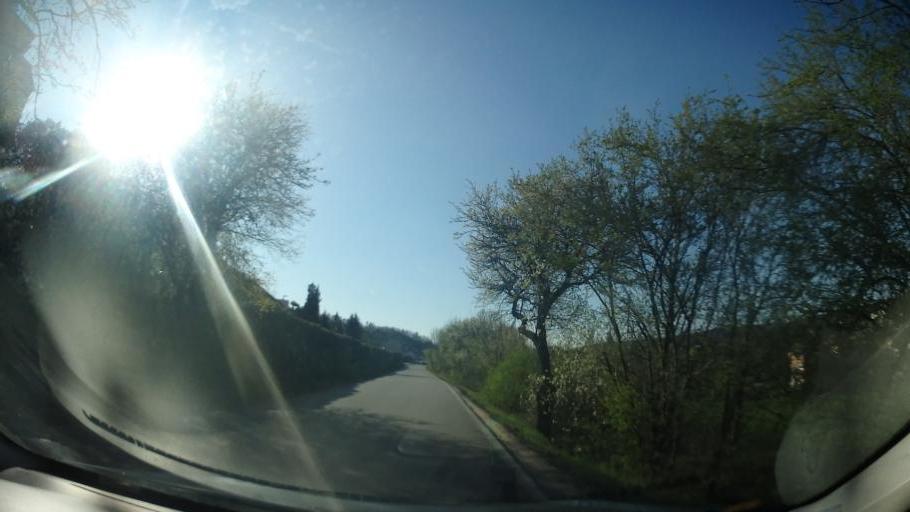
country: CZ
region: South Moravian
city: Ostopovice
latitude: 49.1590
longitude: 16.5514
